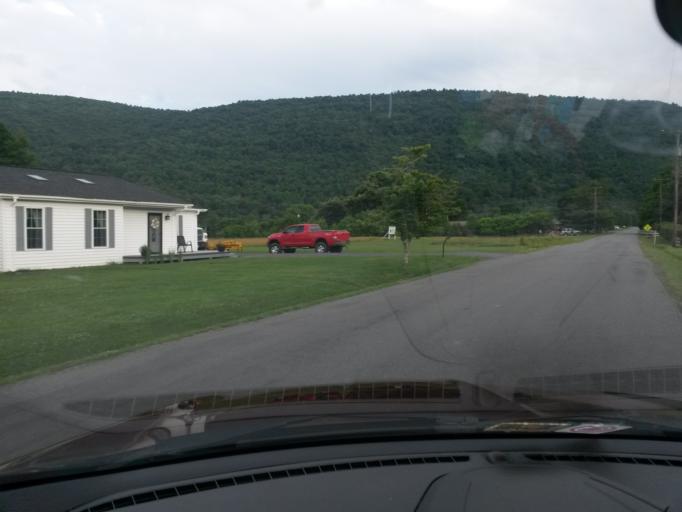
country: US
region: Virginia
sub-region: City of Covington
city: Fairlawn
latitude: 37.7666
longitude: -79.9676
